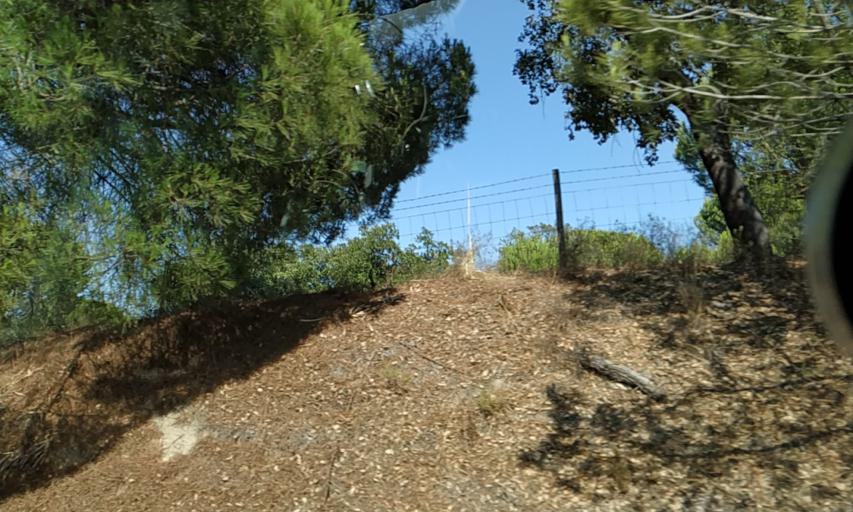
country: PT
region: Santarem
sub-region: Coruche
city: Coruche
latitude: 38.8611
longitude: -8.5444
